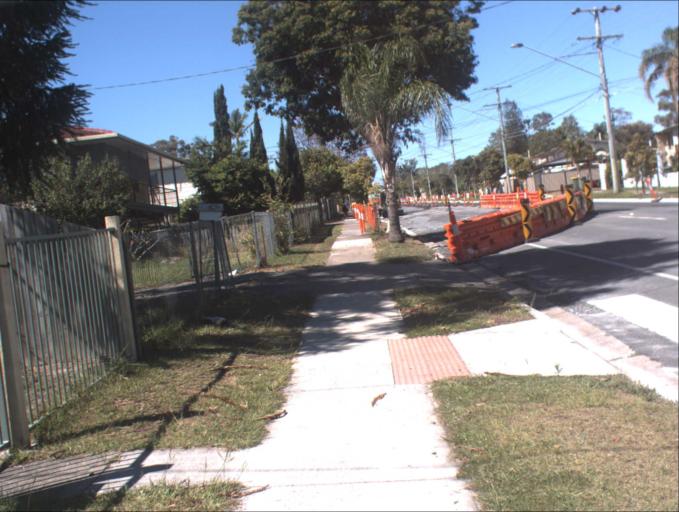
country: AU
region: Queensland
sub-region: Logan
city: Woodridge
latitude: -27.6239
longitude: 153.1105
